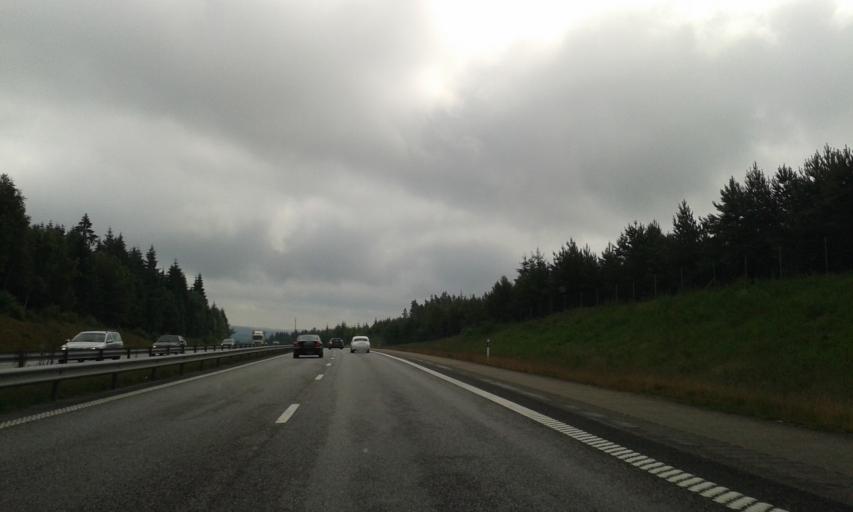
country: SE
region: Vaestra Goetaland
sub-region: Harryda Kommun
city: Hindas
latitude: 57.6704
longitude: 12.4350
